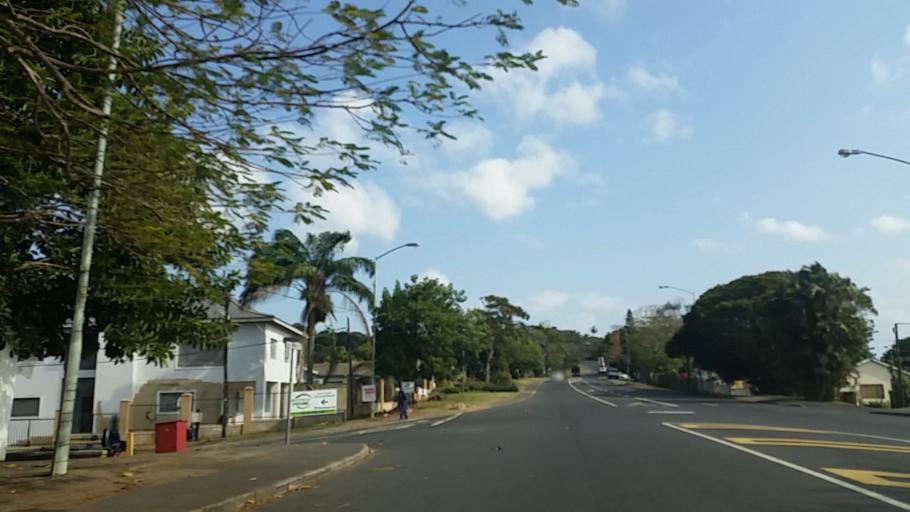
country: ZA
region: KwaZulu-Natal
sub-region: eThekwini Metropolitan Municipality
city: Berea
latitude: -29.8278
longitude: 30.9278
